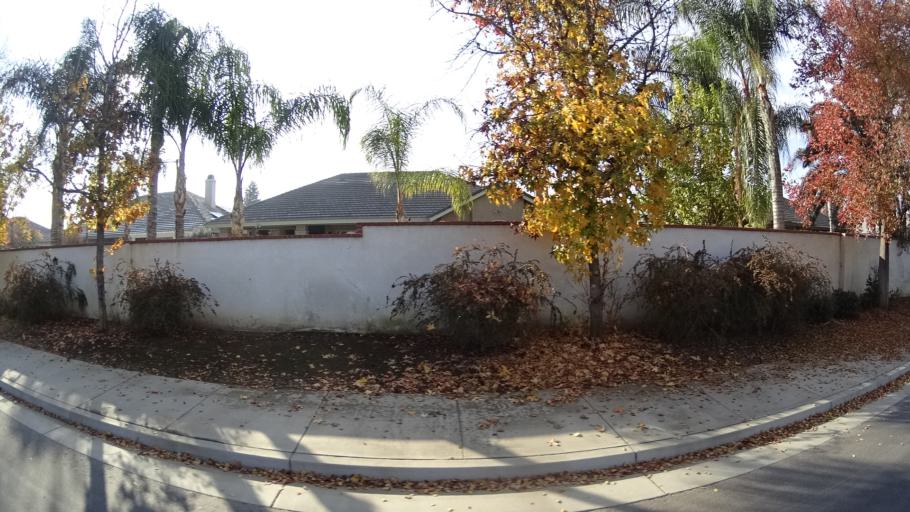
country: US
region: California
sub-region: Kern County
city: Rosedale
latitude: 35.3689
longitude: -119.1577
